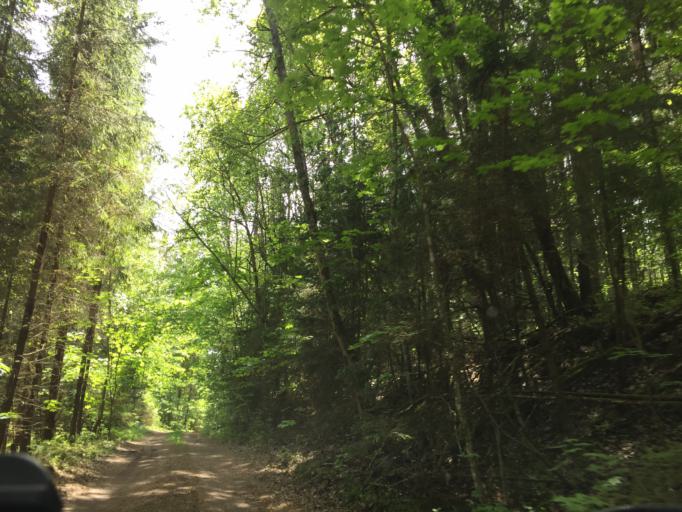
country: LV
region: Koceni
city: Koceni
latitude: 57.4412
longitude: 25.2836
